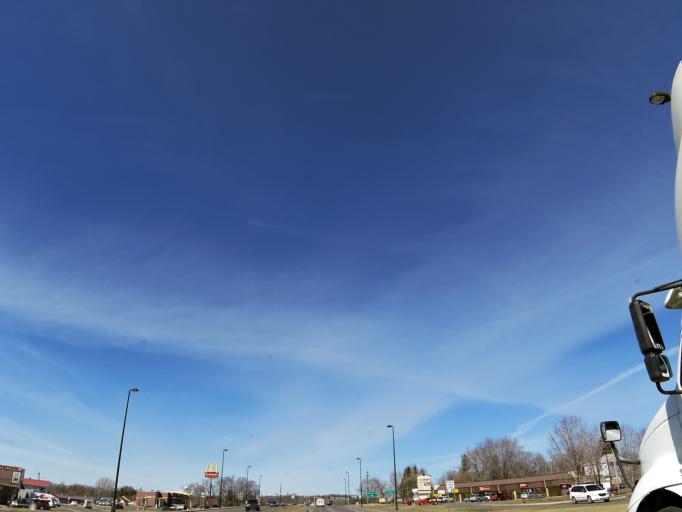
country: US
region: Minnesota
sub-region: Wright County
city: Buffalo
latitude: 45.1787
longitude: -93.8684
